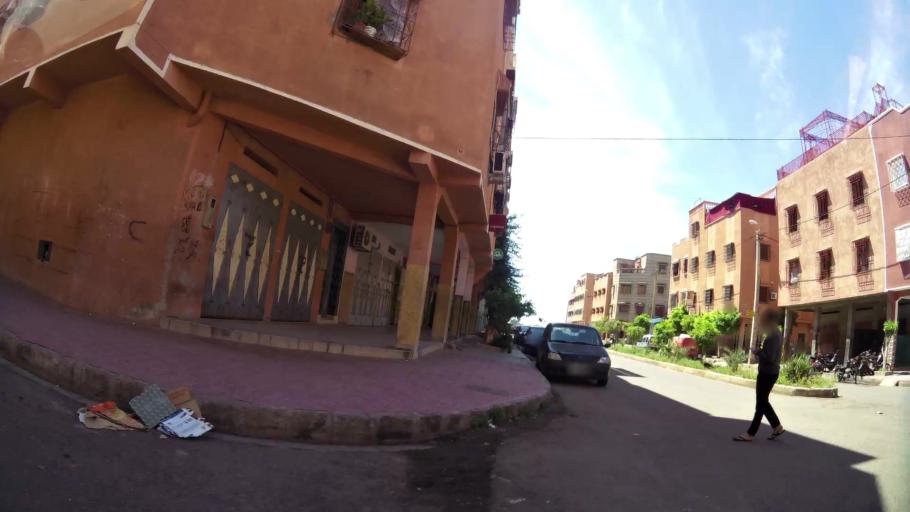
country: MA
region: Marrakech-Tensift-Al Haouz
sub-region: Marrakech
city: Marrakesh
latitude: 31.6441
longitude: -8.0664
